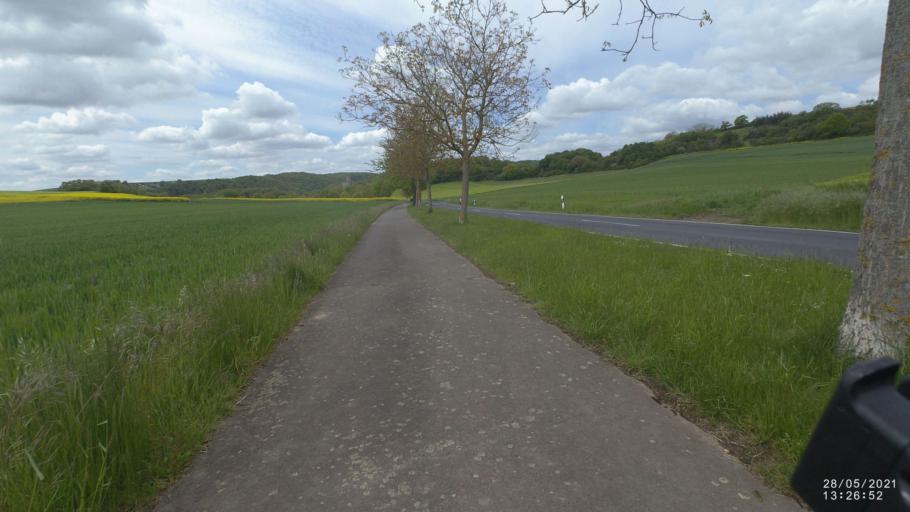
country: DE
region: Rheinland-Pfalz
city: Pillig
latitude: 50.2396
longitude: 7.3041
